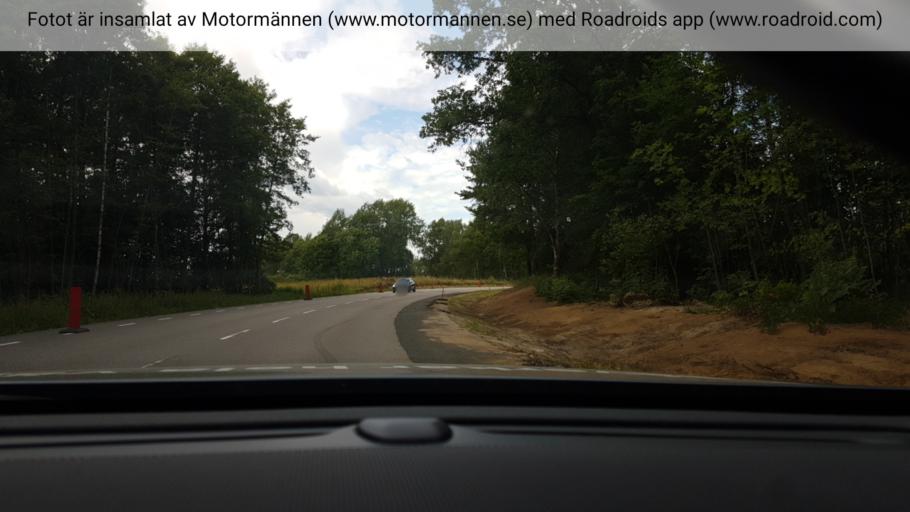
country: SE
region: Skane
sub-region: Hassleholms Kommun
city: Hassleholm
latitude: 56.1741
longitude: 13.7776
